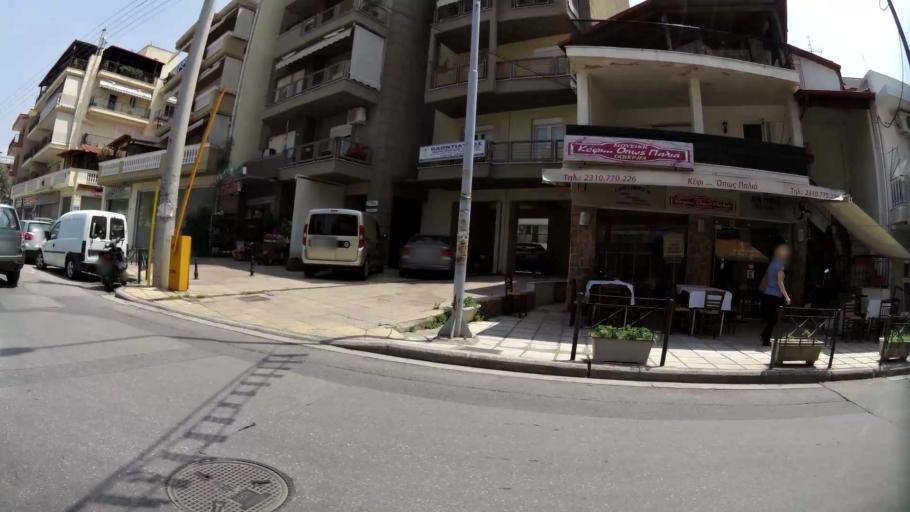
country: GR
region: Central Macedonia
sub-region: Nomos Thessalonikis
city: Evosmos
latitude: 40.6659
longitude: 22.9088
